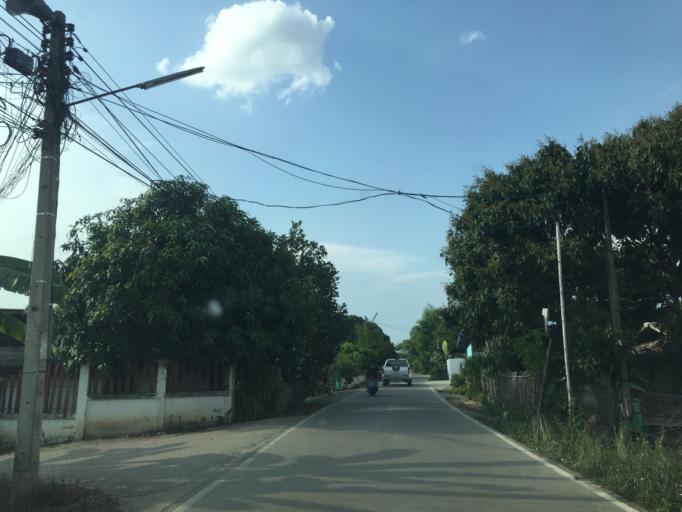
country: TH
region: Lamphun
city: Ban Thi
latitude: 18.6356
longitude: 99.0537
